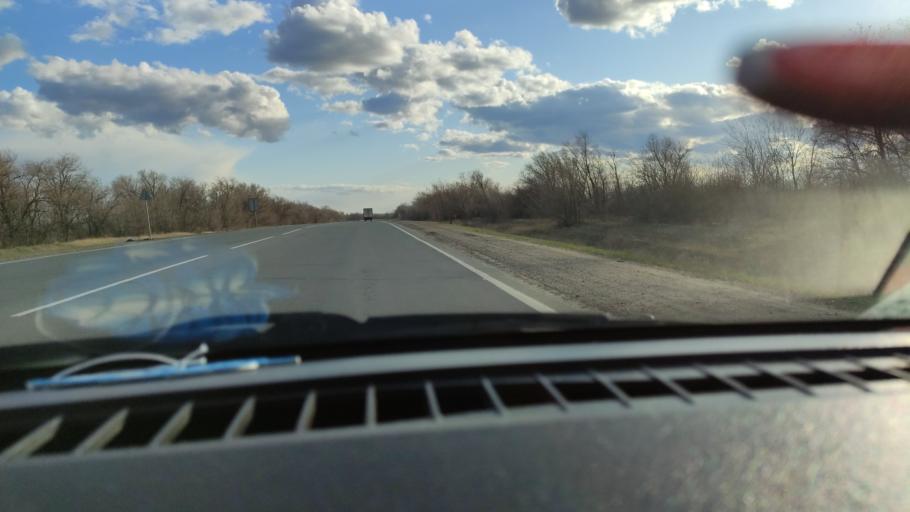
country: RU
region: Saratov
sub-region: Saratovskiy Rayon
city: Saratov
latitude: 51.7103
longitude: 46.0183
